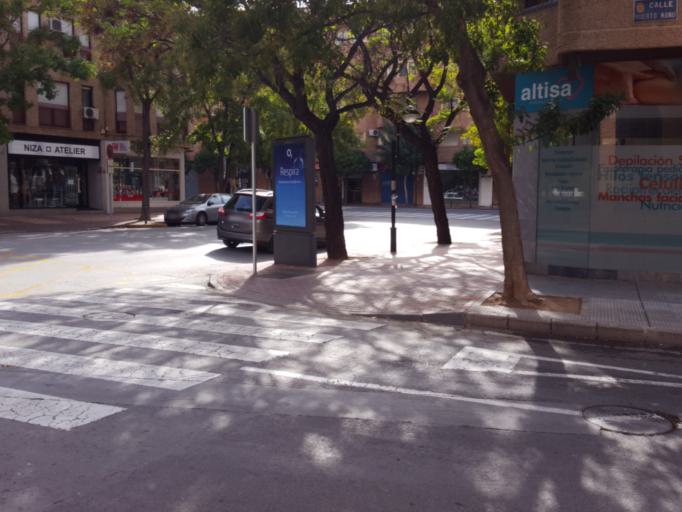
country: ES
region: Murcia
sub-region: Murcia
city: Murcia
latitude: 37.9901
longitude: -1.1393
